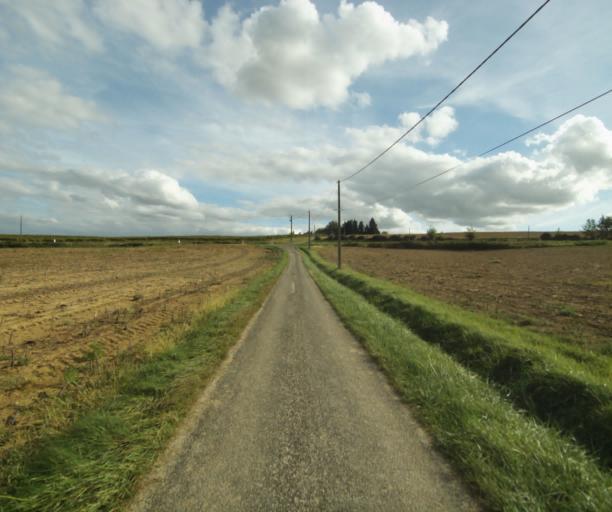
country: FR
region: Midi-Pyrenees
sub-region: Departement du Gers
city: Gondrin
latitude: 43.8454
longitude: 0.2753
